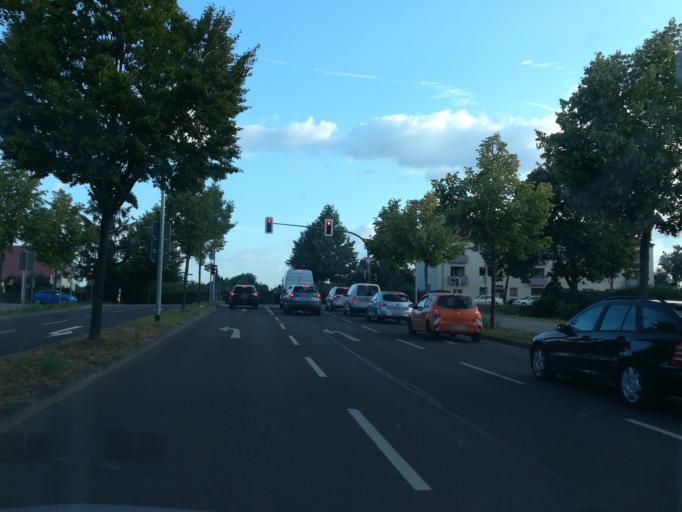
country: DE
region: Saxony-Anhalt
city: Magdeburg
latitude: 52.1385
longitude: 11.6029
